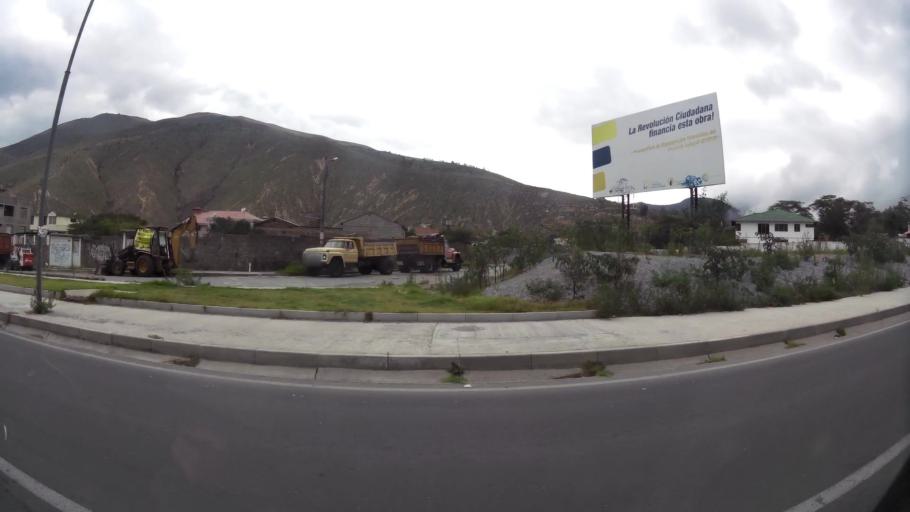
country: EC
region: Pichincha
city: Quito
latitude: -0.0073
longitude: -78.4530
